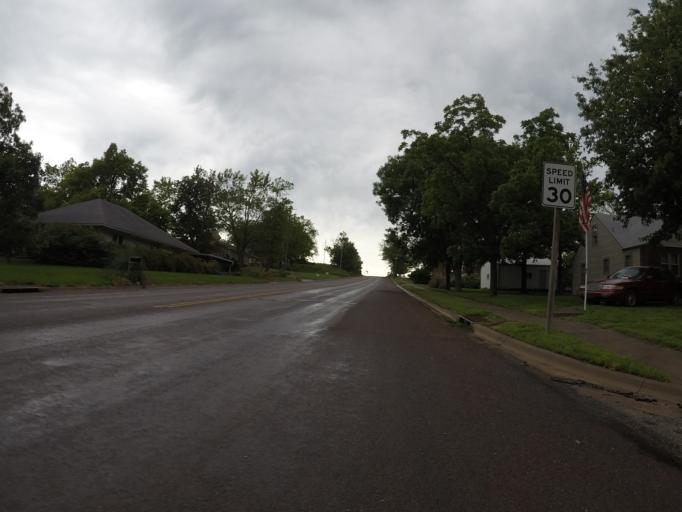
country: US
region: Kansas
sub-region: Wabaunsee County
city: Alma
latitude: 38.8600
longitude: -96.1112
